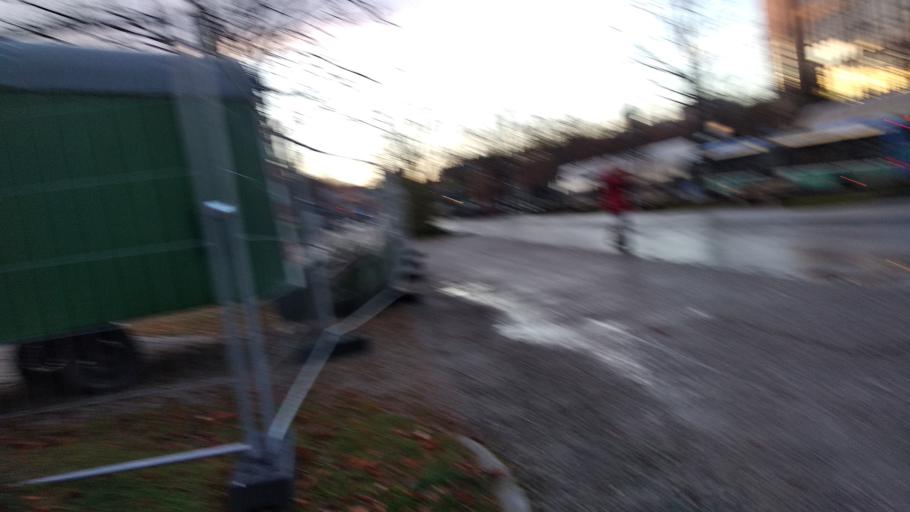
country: DE
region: Bavaria
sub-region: Upper Bavaria
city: Neubiberg
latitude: 48.1008
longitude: 11.6477
